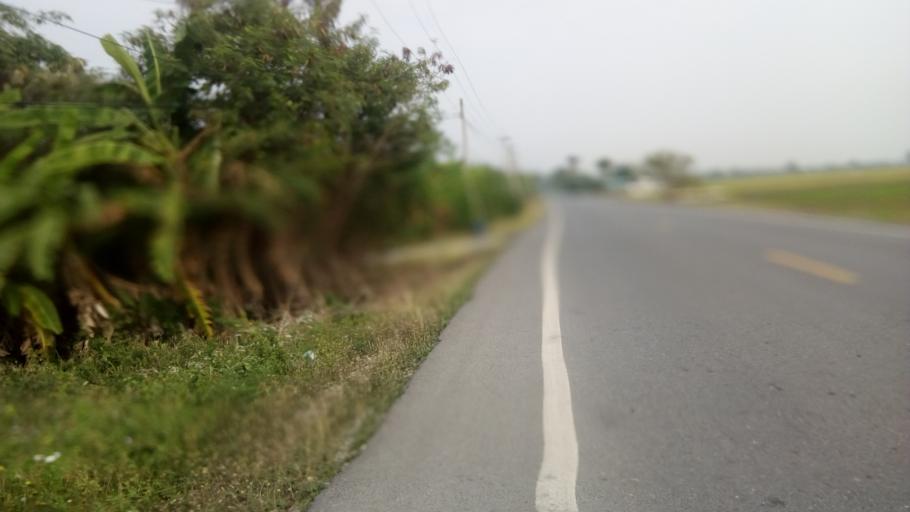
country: TH
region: Pathum Thani
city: Ban Rangsit
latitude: 14.0276
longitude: 100.8242
